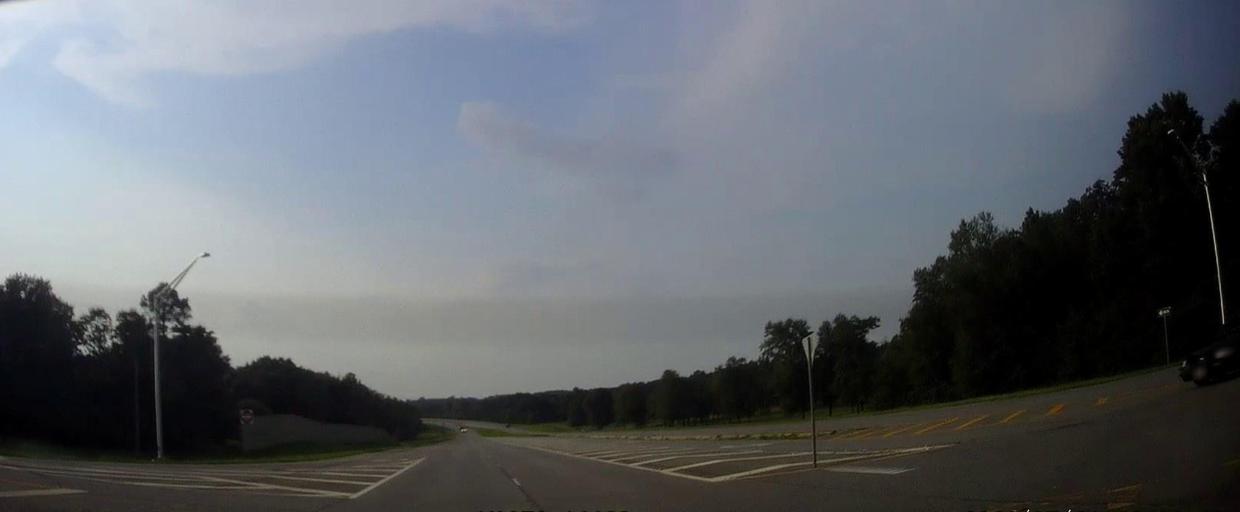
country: US
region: Georgia
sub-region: Laurens County
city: Dublin
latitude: 32.5349
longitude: -82.9699
